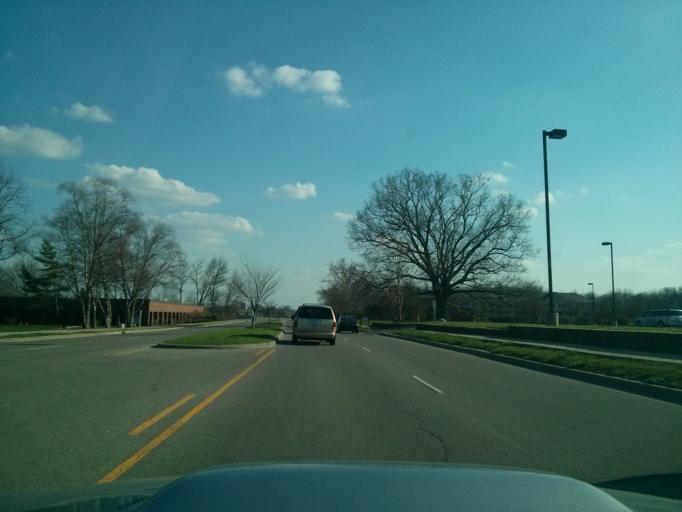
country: US
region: Indiana
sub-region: Hamilton County
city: Carmel
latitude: 39.9545
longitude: -86.1552
